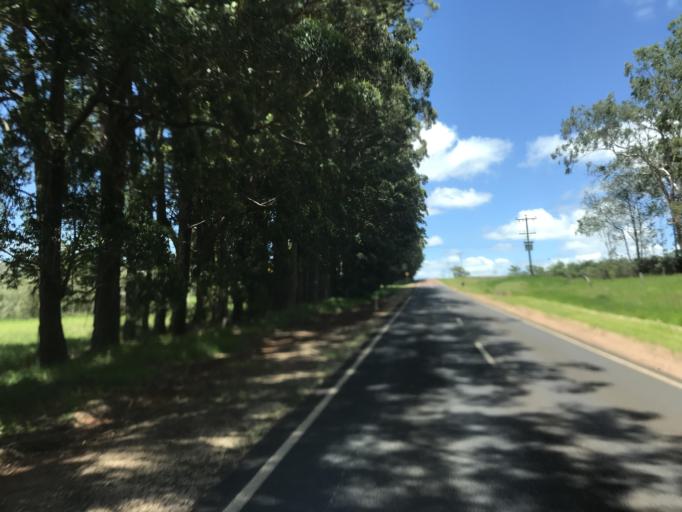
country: AU
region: Queensland
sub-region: Tablelands
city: Ravenshoe
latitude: -17.5325
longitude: 145.4530
